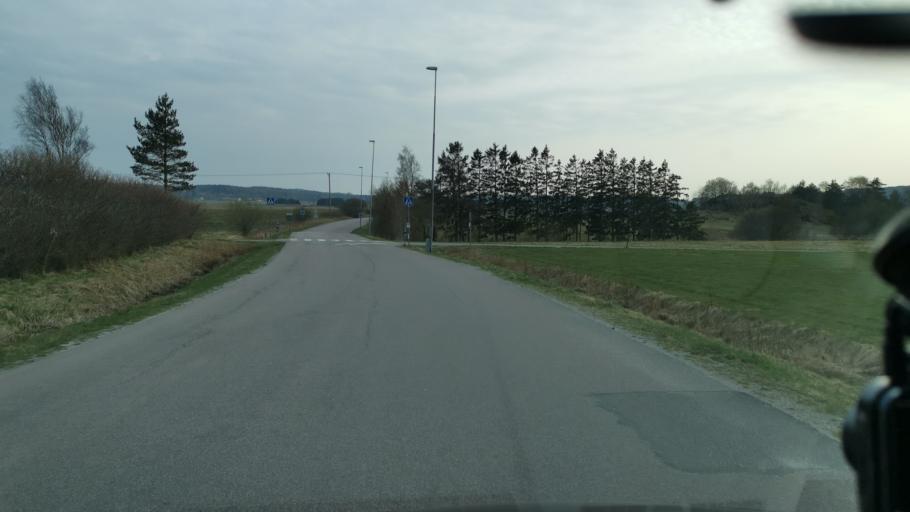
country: SE
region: Vaestra Goetaland
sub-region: Kungalvs Kommun
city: Kode
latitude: 57.9437
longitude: 11.8364
